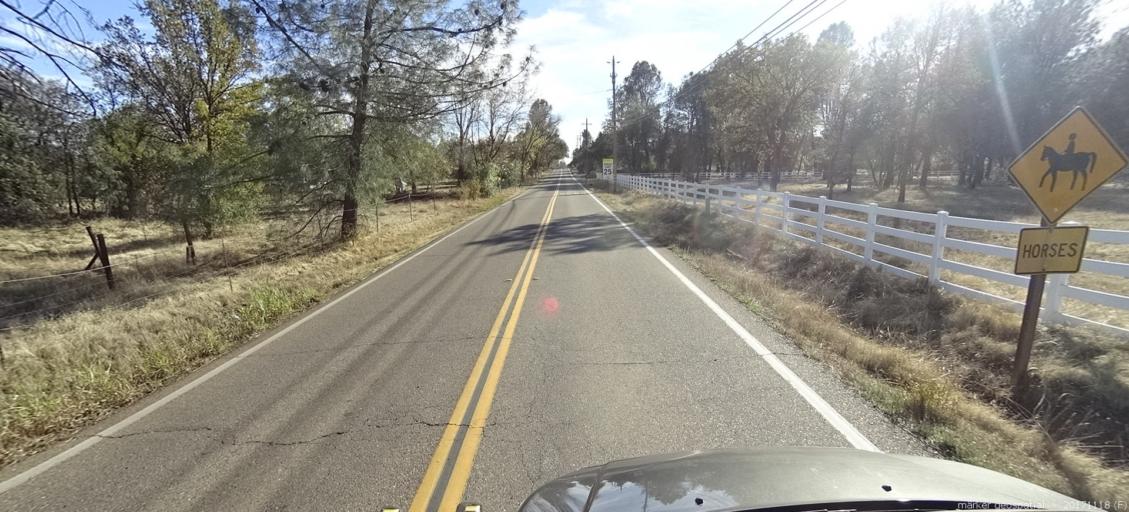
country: US
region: California
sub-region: Shasta County
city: Redding
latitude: 40.4769
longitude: -122.4548
